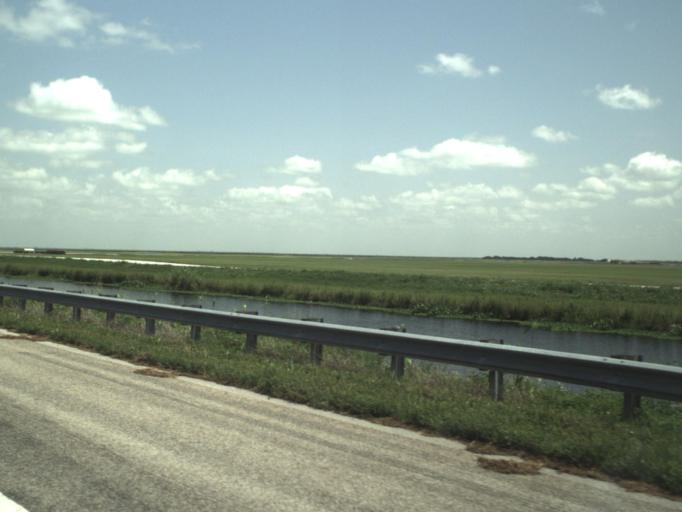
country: US
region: Florida
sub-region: Palm Beach County
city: Belle Glade Camp
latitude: 26.5668
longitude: -80.7104
